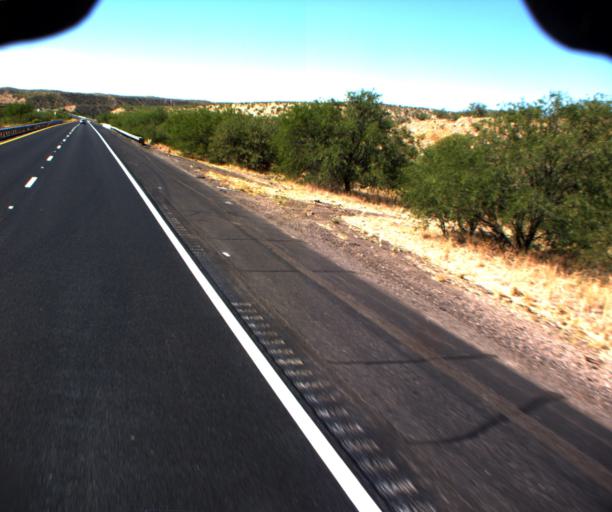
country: US
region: Arizona
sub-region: Santa Cruz County
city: Tubac
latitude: 31.5582
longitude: -111.0515
